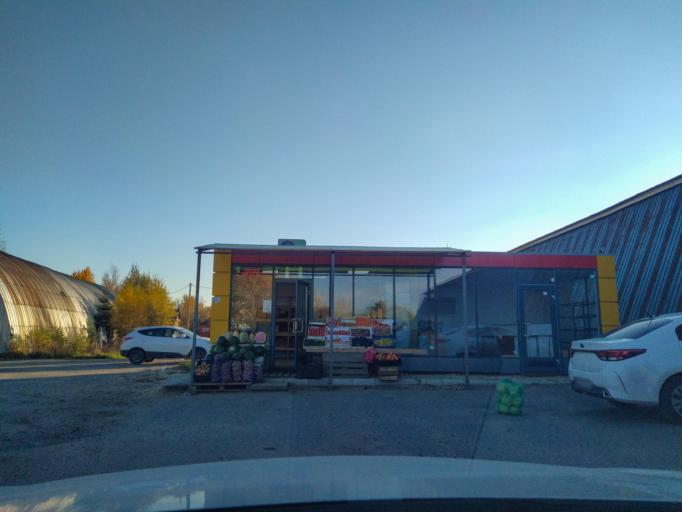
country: RU
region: Leningrad
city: Siverskiy
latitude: 59.3558
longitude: 30.0605
